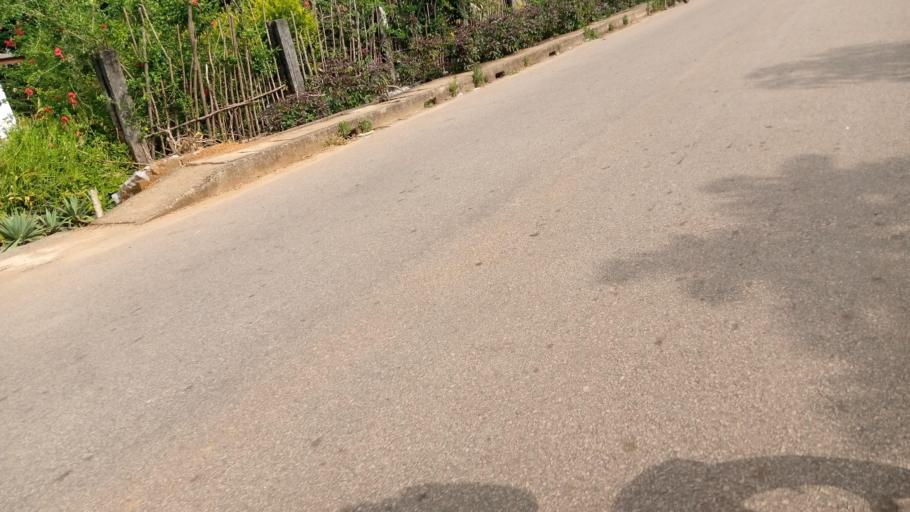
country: SL
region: Southern Province
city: Pujehun
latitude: 7.3500
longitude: -11.7189
